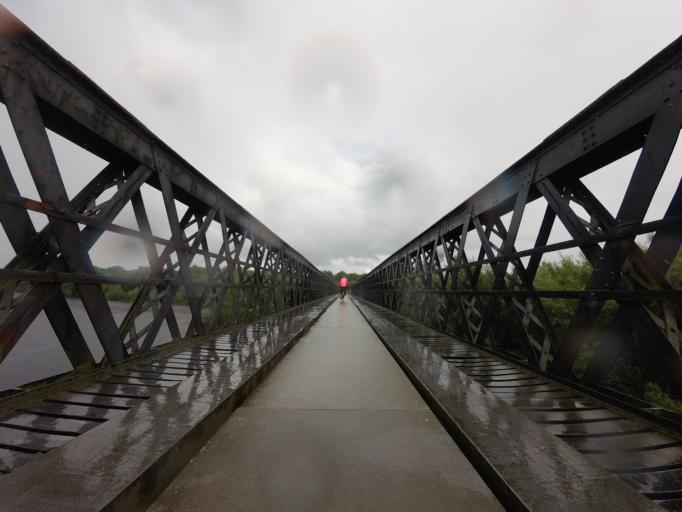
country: GB
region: Scotland
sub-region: Moray
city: Fochabers
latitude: 57.6628
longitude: -3.0972
